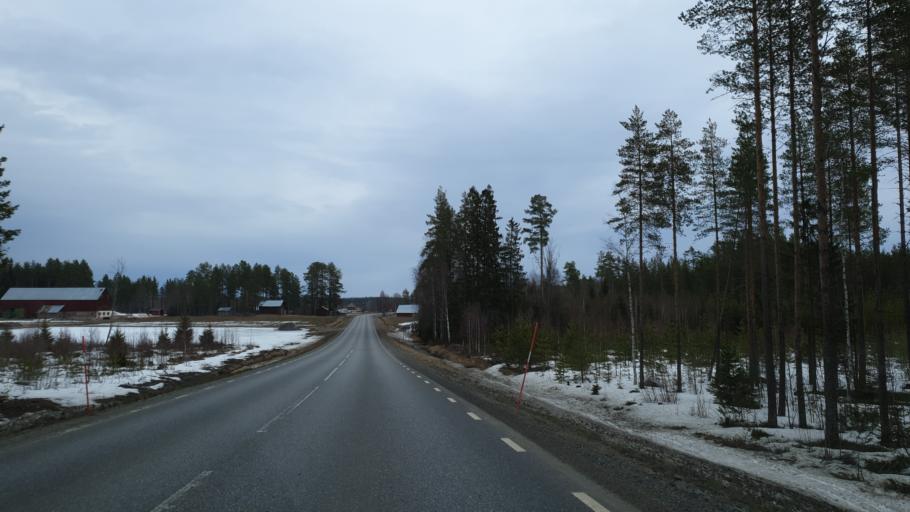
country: SE
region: Vaesterbotten
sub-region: Robertsfors Kommun
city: Robertsfors
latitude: 64.2277
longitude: 20.9413
